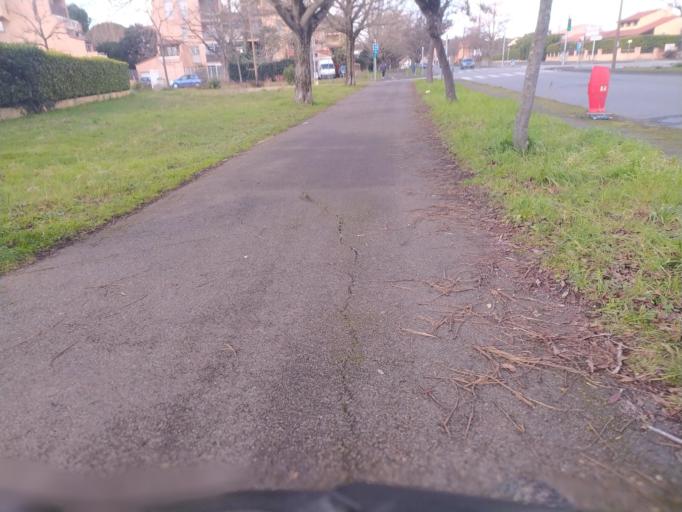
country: FR
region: Midi-Pyrenees
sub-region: Departement de la Haute-Garonne
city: Blagnac
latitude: 43.5798
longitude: 1.3914
